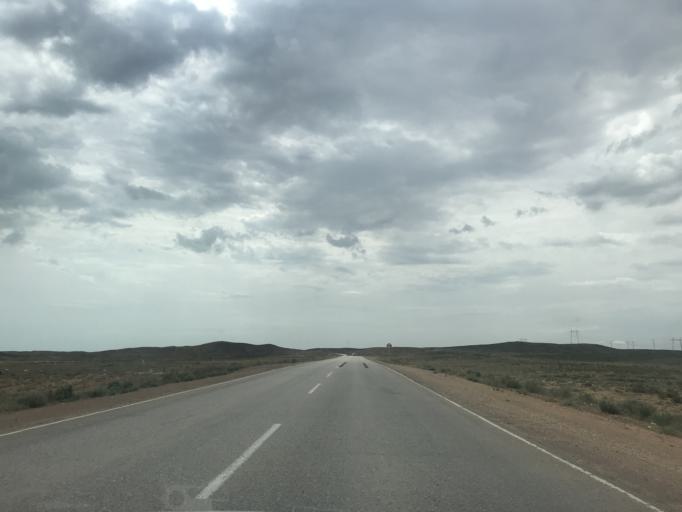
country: KZ
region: Zhambyl
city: Mynaral
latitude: 45.5168
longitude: 73.4922
